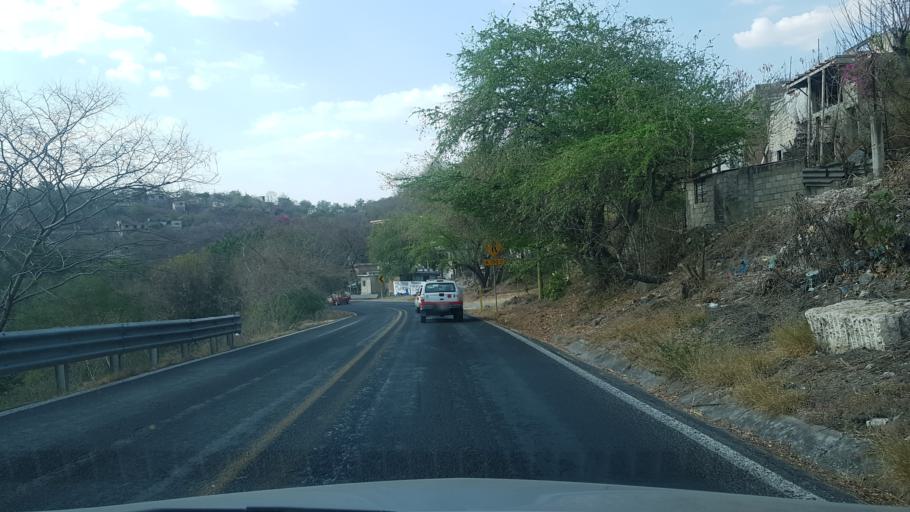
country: MX
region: Morelos
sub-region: Amacuzac
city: Amacuzac
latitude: 18.6037
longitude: -99.3673
